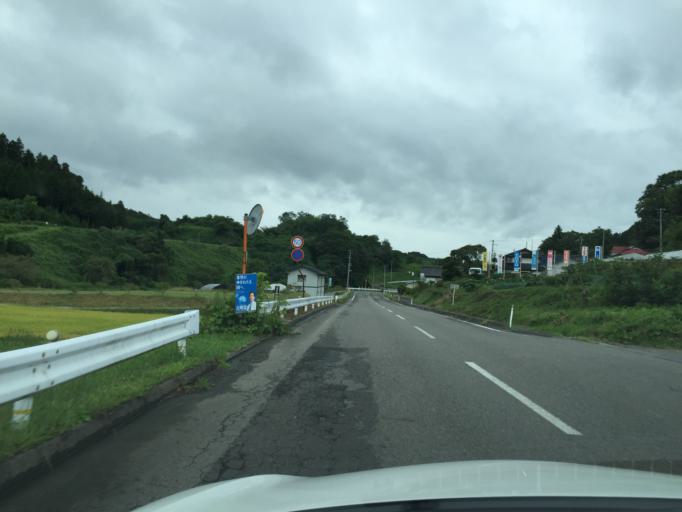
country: JP
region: Fukushima
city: Funehikimachi-funehiki
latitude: 37.4587
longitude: 140.5320
